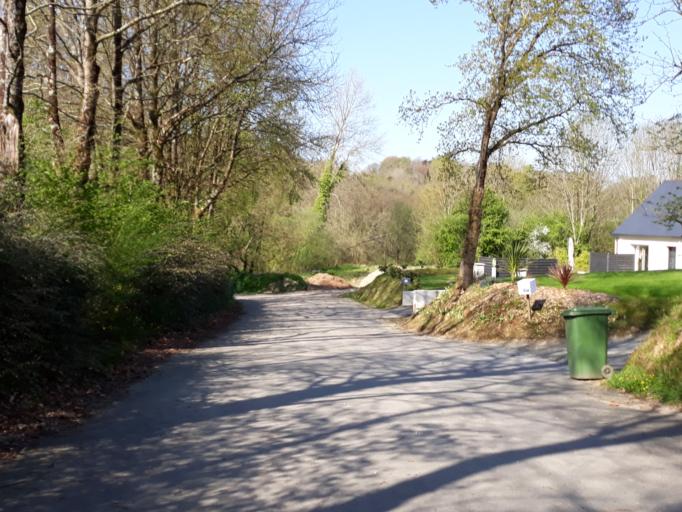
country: FR
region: Brittany
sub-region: Departement du Finistere
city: Sizun
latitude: 48.4043
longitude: -4.0828
